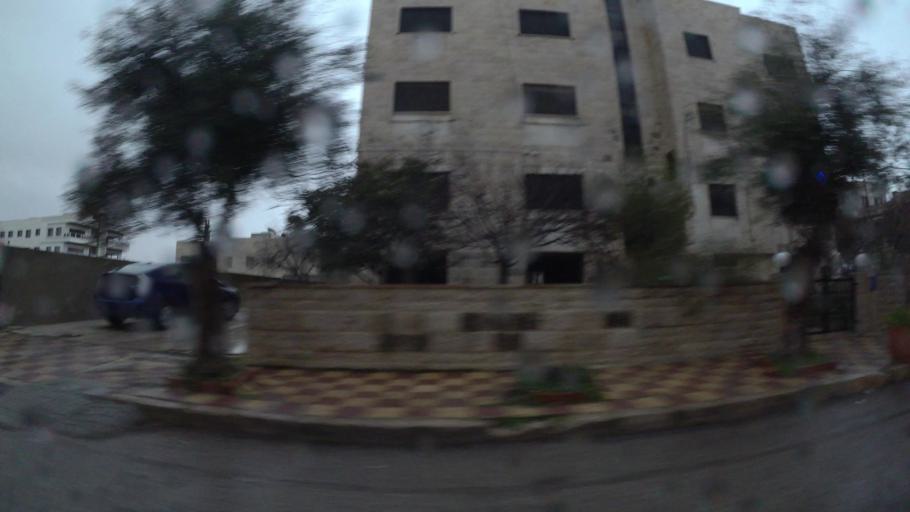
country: JO
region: Amman
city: Umm as Summaq
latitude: 31.9061
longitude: 35.8548
